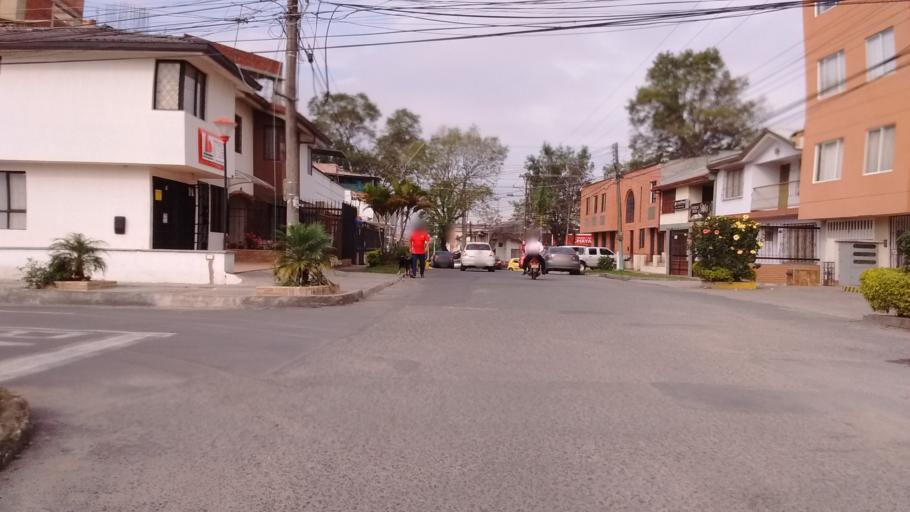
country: CO
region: Cauca
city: Popayan
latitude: 2.4537
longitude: -76.5968
